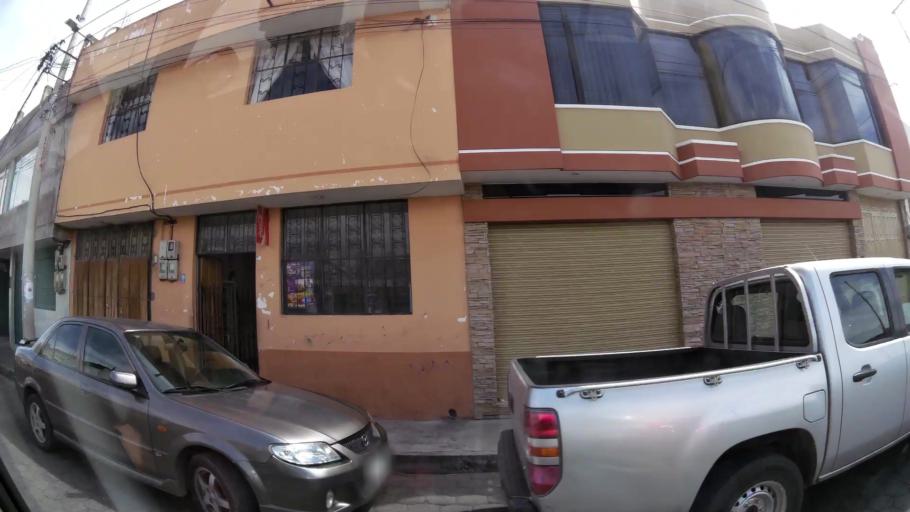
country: EC
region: Cotopaxi
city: Latacunga
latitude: -0.9278
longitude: -78.6084
